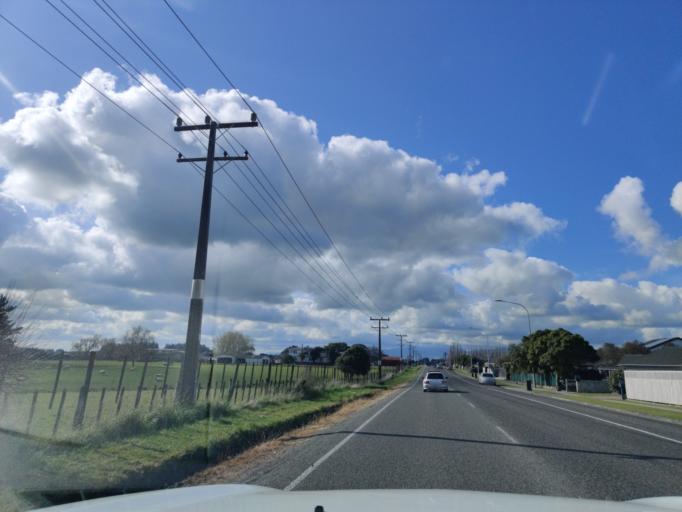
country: NZ
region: Manawatu-Wanganui
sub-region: Palmerston North City
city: Palmerston North
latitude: -40.3201
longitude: 175.6533
